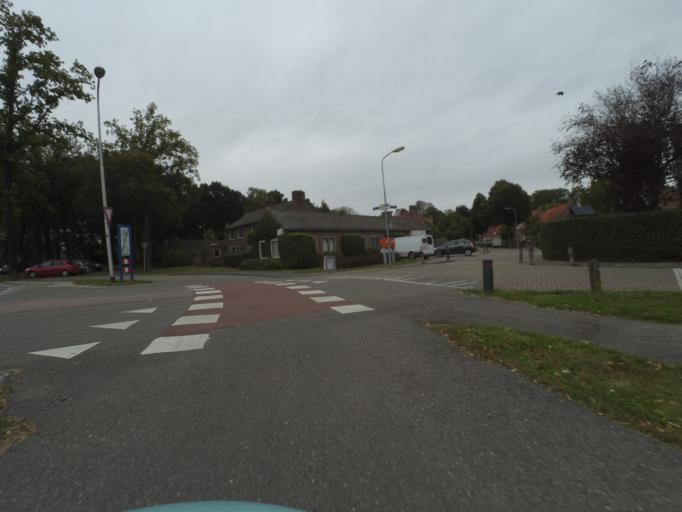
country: NL
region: Gelderland
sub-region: Gemeente Geldermalsen
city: Geldermalsen
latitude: 51.9143
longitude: 5.3317
